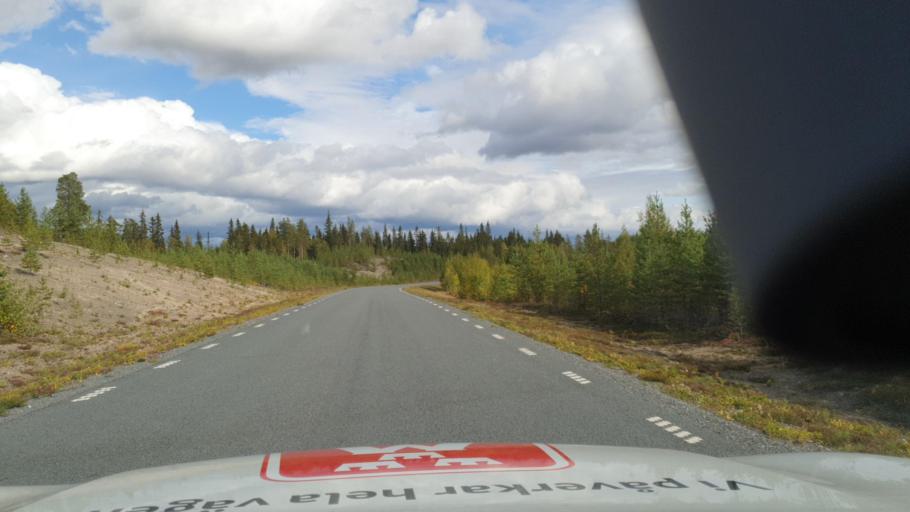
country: SE
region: Dalarna
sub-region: Alvdalens Kommun
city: AElvdalen
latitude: 61.6791
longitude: 13.3586
